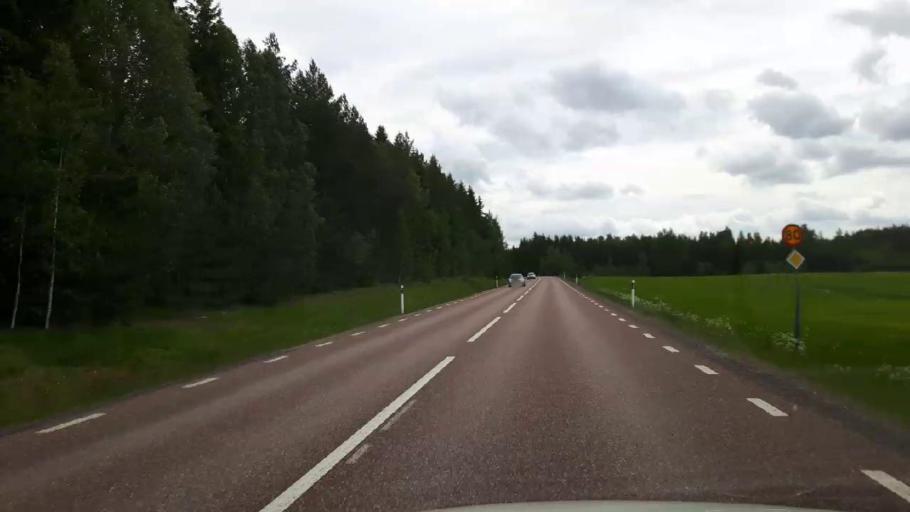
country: SE
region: Dalarna
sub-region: Hedemora Kommun
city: Brunna
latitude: 60.2107
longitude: 15.9917
